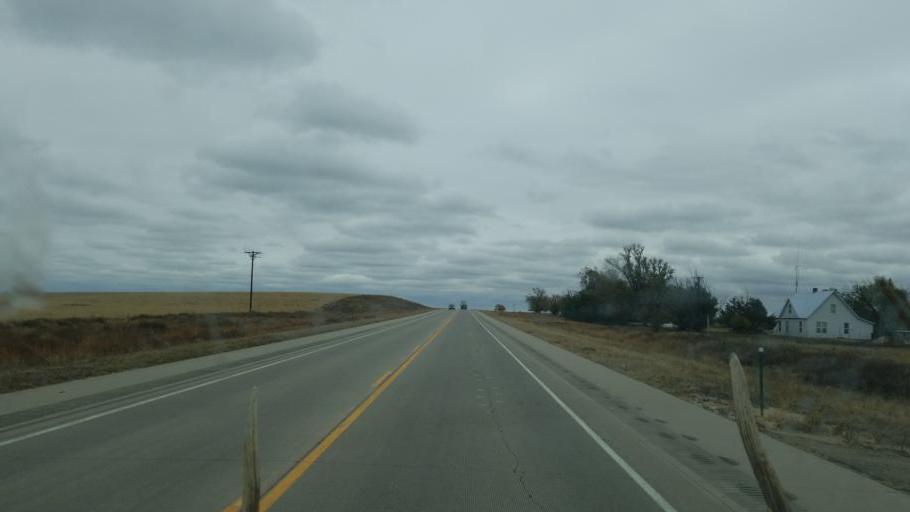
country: US
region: Colorado
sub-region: Kiowa County
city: Eads
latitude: 38.7277
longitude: -102.7762
